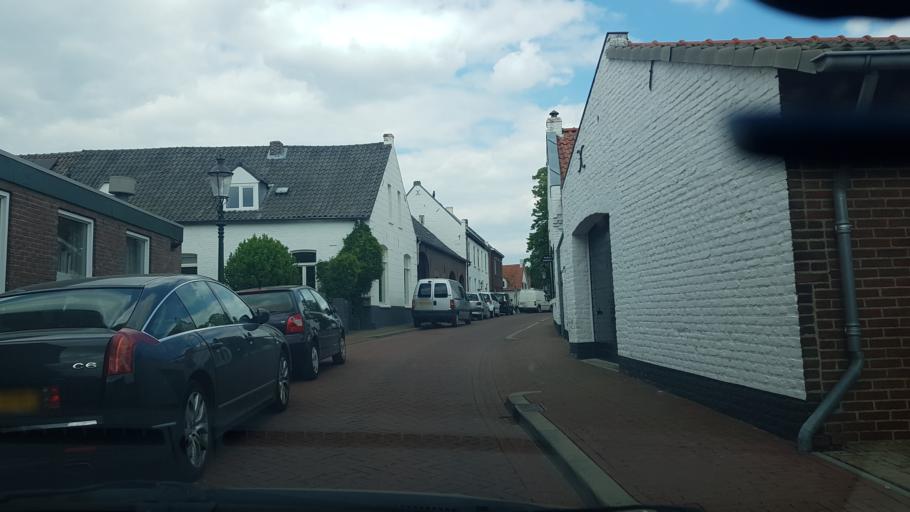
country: NL
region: Limburg
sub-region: Gemeente Roerdalen
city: Sint Odilienberg
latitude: 51.1467
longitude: 6.0014
